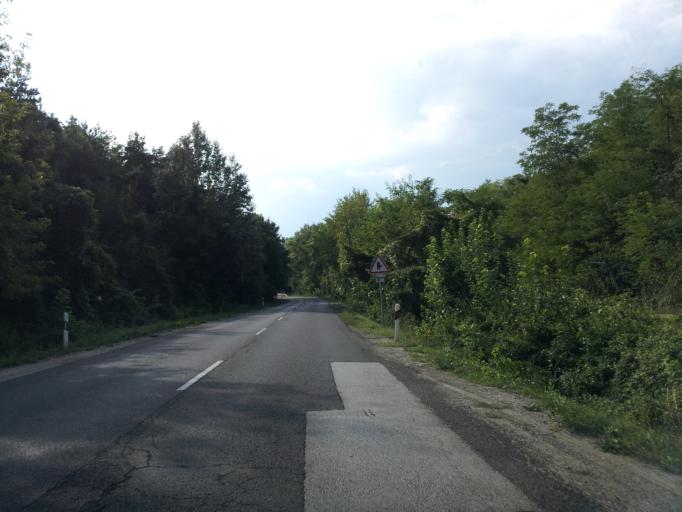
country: HU
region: Pest
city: Dunabogdany
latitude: 47.8133
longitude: 19.0812
